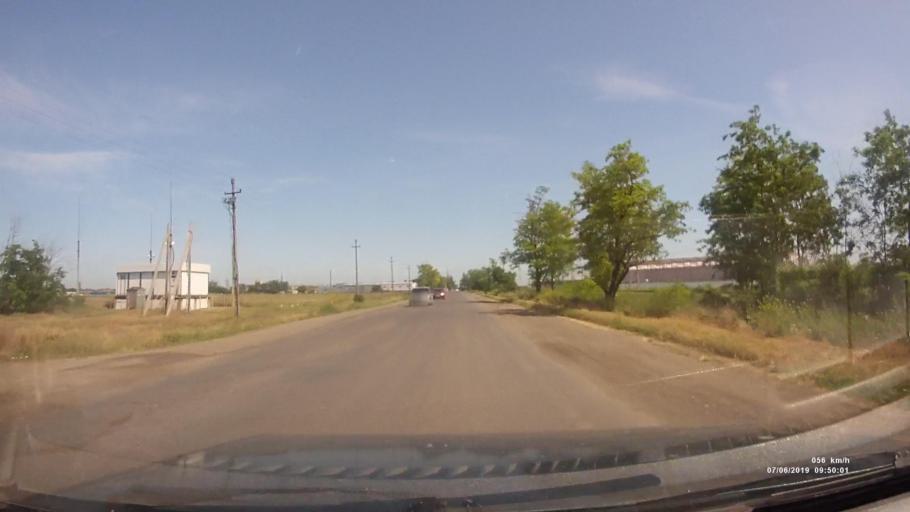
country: RU
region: Rostov
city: Azov
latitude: 47.0757
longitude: 39.4377
